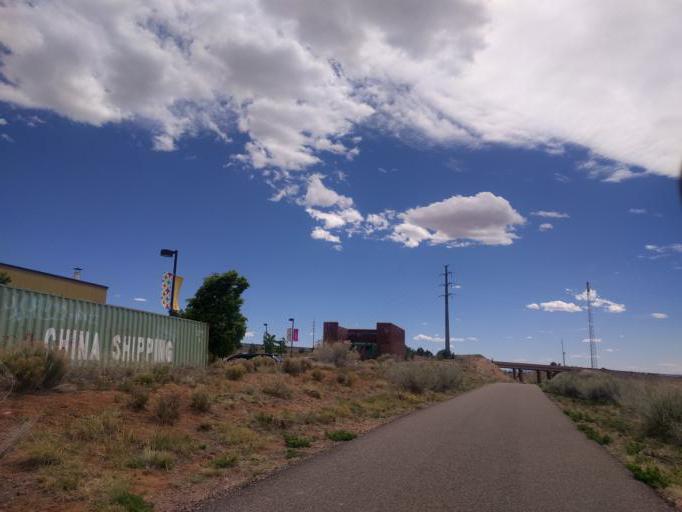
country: US
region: New Mexico
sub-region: Santa Fe County
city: Santa Fe
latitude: 35.6338
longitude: -105.9639
